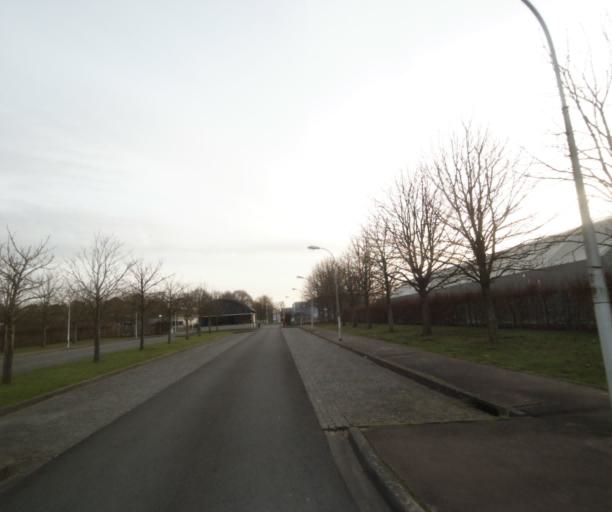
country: FR
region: Pays de la Loire
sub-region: Departement de la Sarthe
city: Arnage
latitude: 47.9447
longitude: 0.2139
